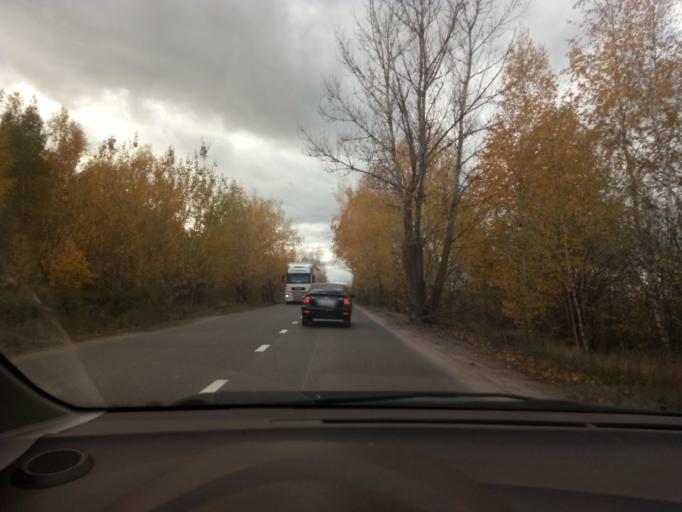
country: RU
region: Tatarstan
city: Staroye Arakchino
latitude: 55.8847
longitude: 48.9958
